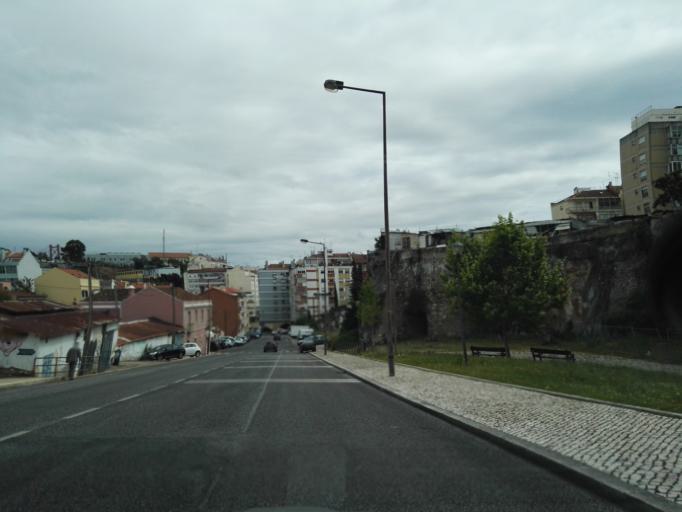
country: PT
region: Lisbon
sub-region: Oeiras
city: Alges
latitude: 38.7056
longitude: -9.1926
